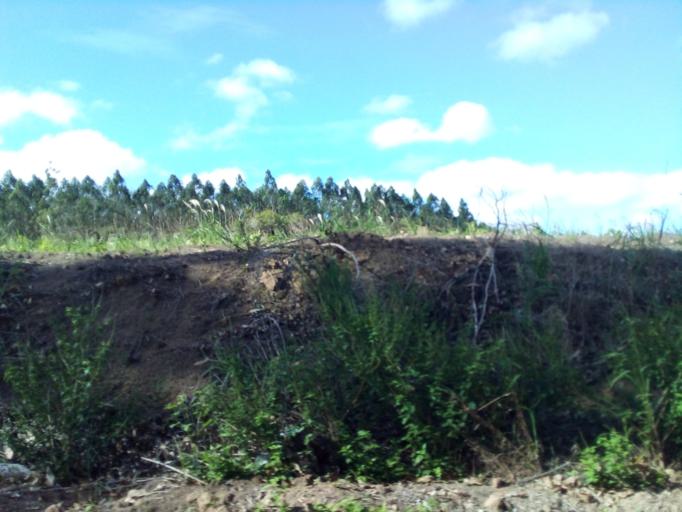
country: BR
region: Espirito Santo
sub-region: Aracruz
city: Aracruz
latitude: -19.7126
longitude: -40.2119
